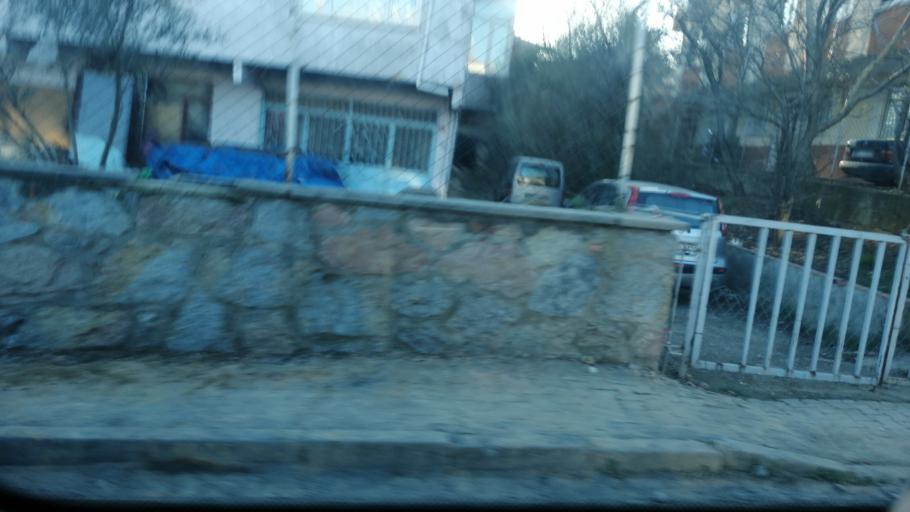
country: TR
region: Istanbul
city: UEskuedar
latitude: 41.0565
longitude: 29.0666
